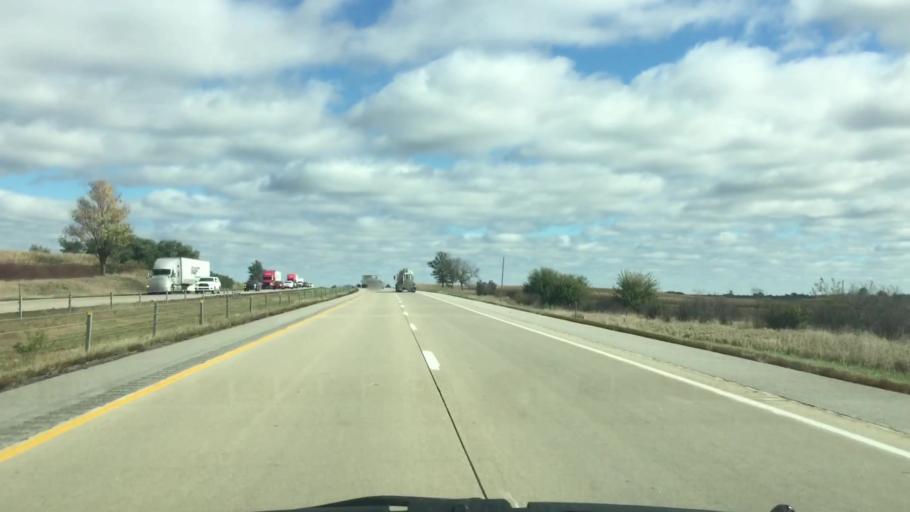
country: US
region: Iowa
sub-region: Poweshiek County
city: Brooklyn
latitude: 41.6950
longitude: -92.4575
